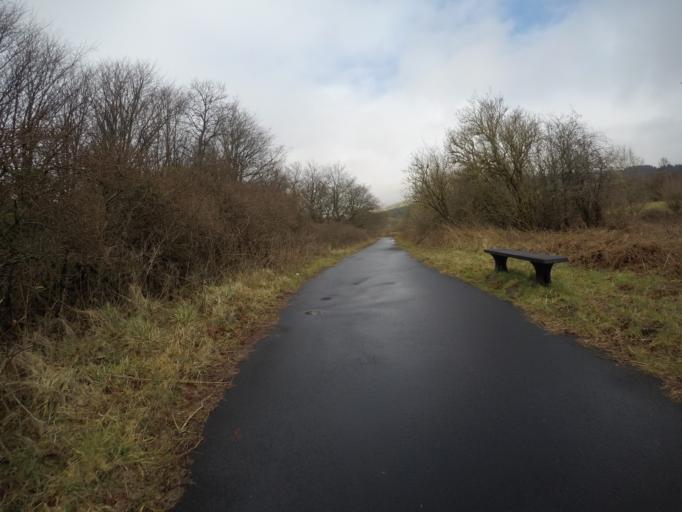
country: GB
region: Scotland
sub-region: North Ayrshire
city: Fairlie
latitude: 55.7332
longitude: -4.8635
